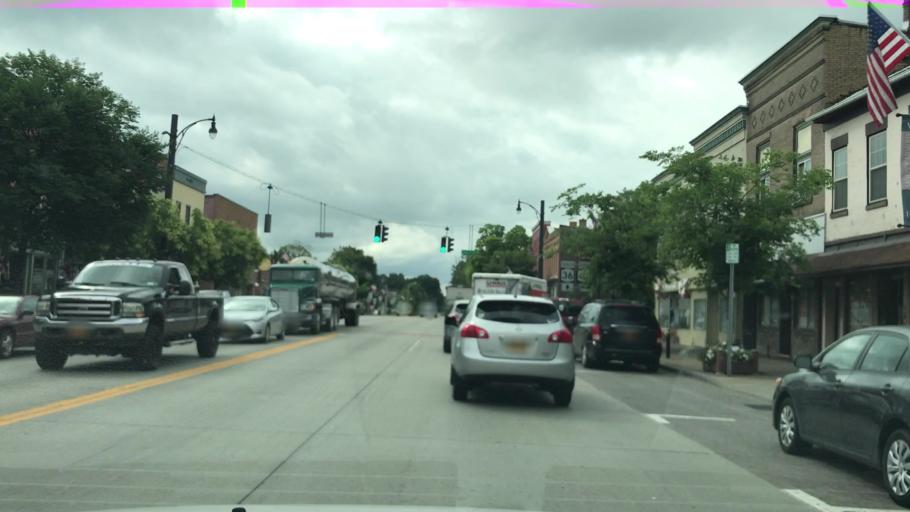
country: US
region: New York
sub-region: Livingston County
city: Mount Morris
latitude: 42.7256
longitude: -77.8741
